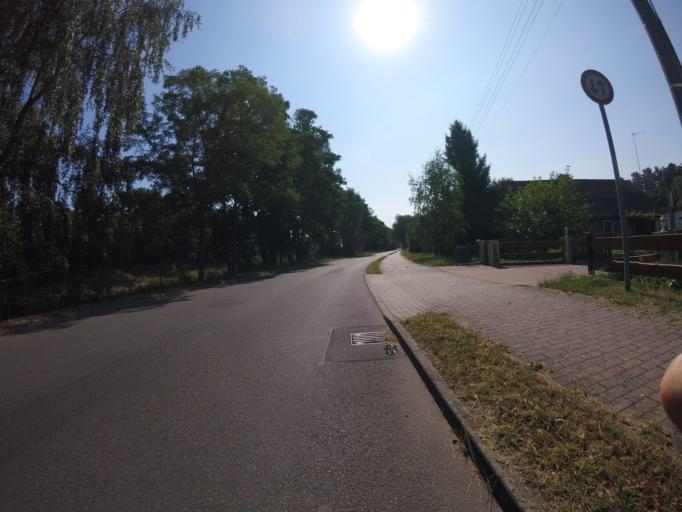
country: DE
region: Brandenburg
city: Mullrose
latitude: 52.2643
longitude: 14.3675
